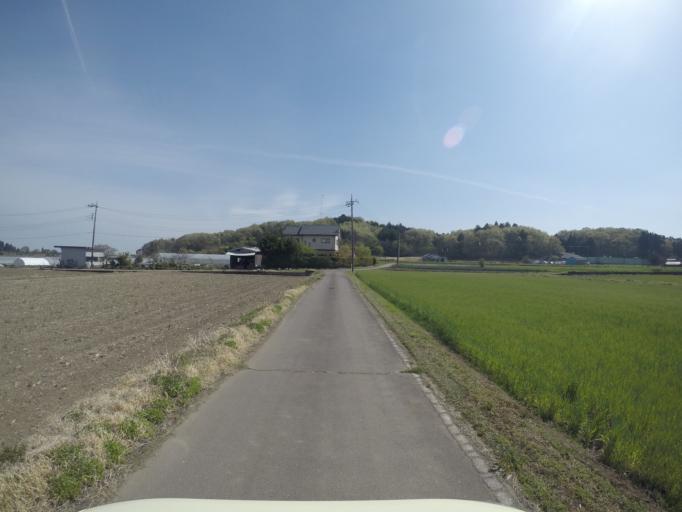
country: JP
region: Tochigi
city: Tochigi
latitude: 36.4519
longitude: 139.7122
